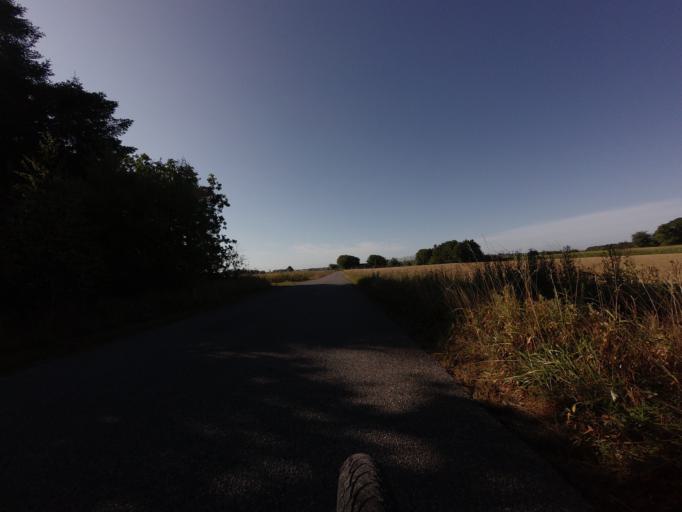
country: DK
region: North Denmark
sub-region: Hjorring Kommune
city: Vra
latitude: 57.3826
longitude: 9.9575
